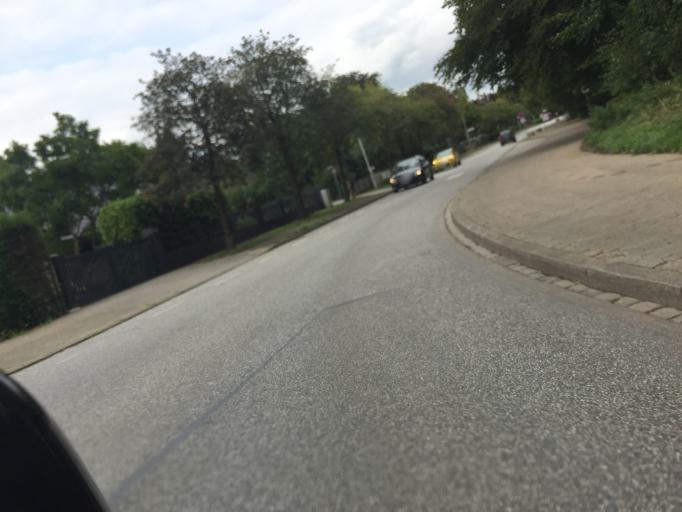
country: DE
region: Schleswig-Holstein
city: Itzehoe
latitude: 53.9358
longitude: 9.5084
